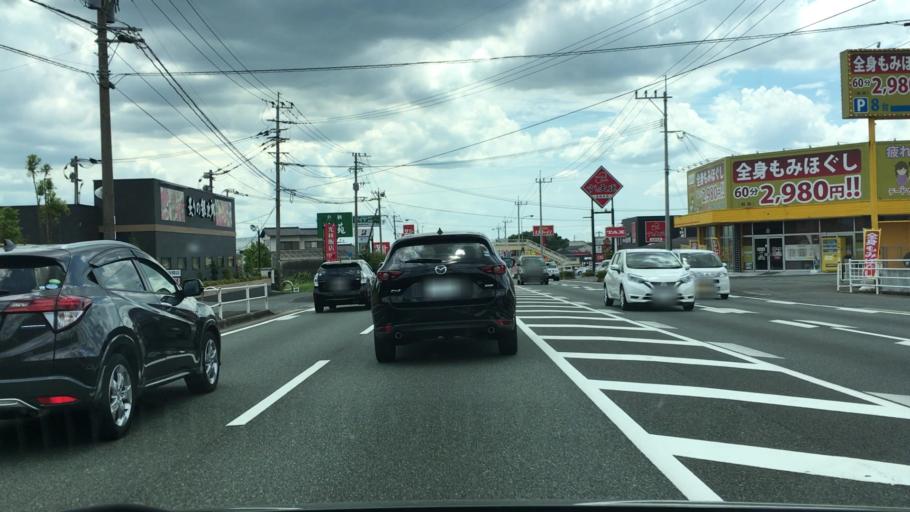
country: JP
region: Saga Prefecture
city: Tosu
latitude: 33.3865
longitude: 130.4997
